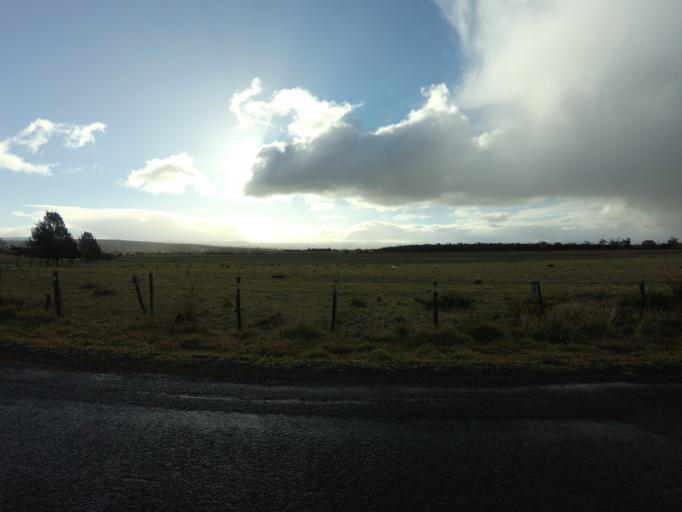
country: AU
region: Tasmania
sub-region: Break O'Day
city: St Helens
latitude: -42.0938
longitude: 148.0733
